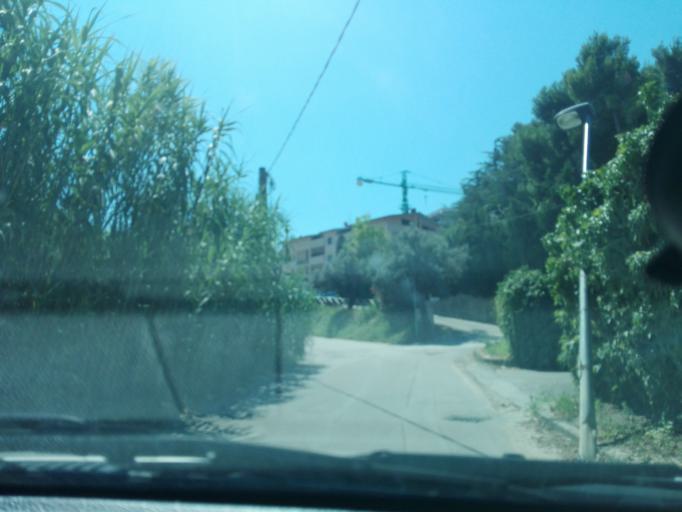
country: IT
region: Abruzzo
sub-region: Provincia di Pescara
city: Montesilvano Marina
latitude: 42.4952
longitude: 14.1606
